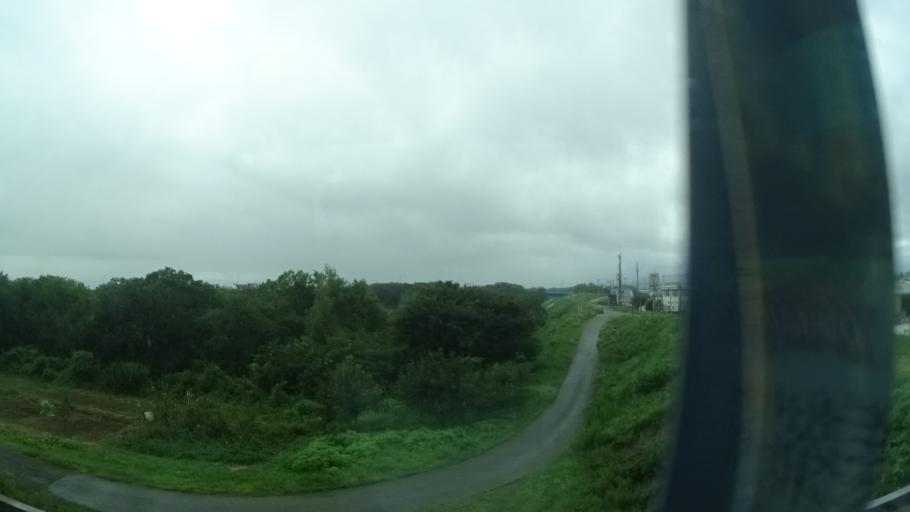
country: JP
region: Yamagata
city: Tsuruoka
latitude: 38.7395
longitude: 139.8481
